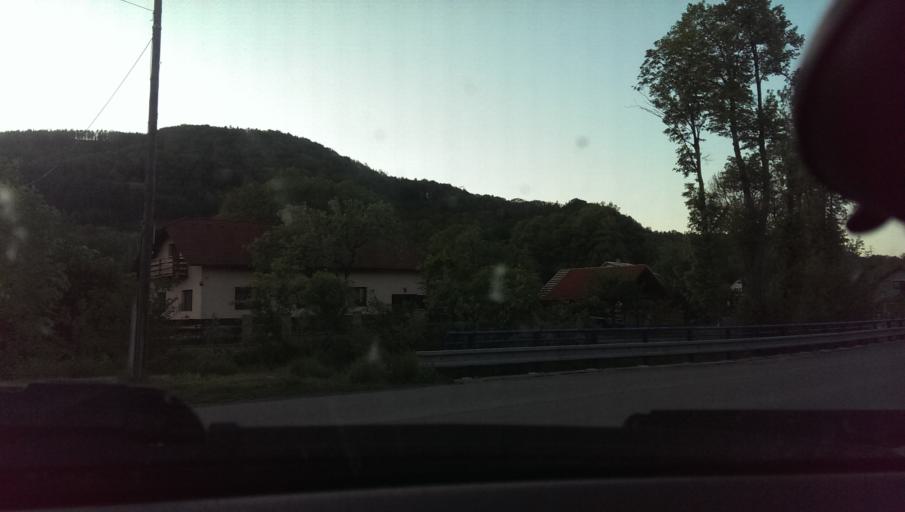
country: CZ
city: Lichnov (o. Novy Jicin)
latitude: 49.5702
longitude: 18.1796
